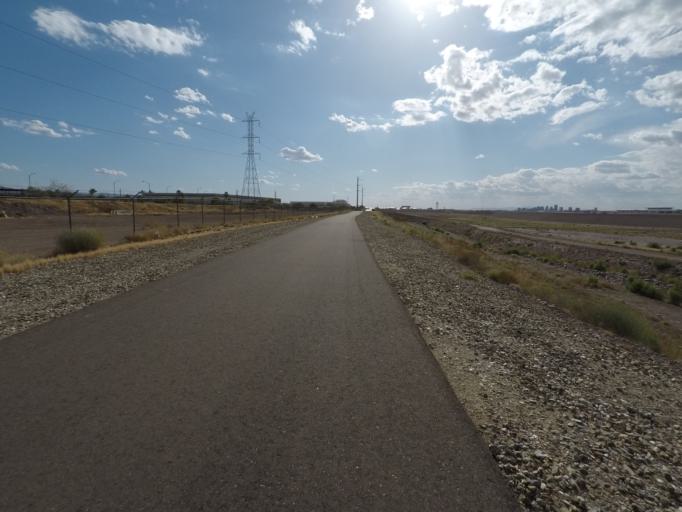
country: US
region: Arizona
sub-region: Maricopa County
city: Tempe Junction
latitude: 33.4263
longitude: -111.9931
